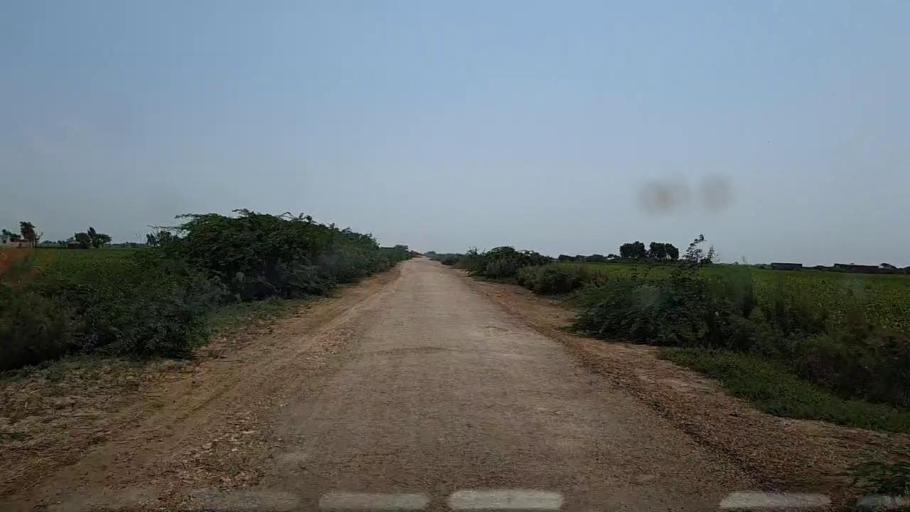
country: PK
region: Sindh
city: Mirpur Batoro
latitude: 24.6276
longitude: 68.4522
